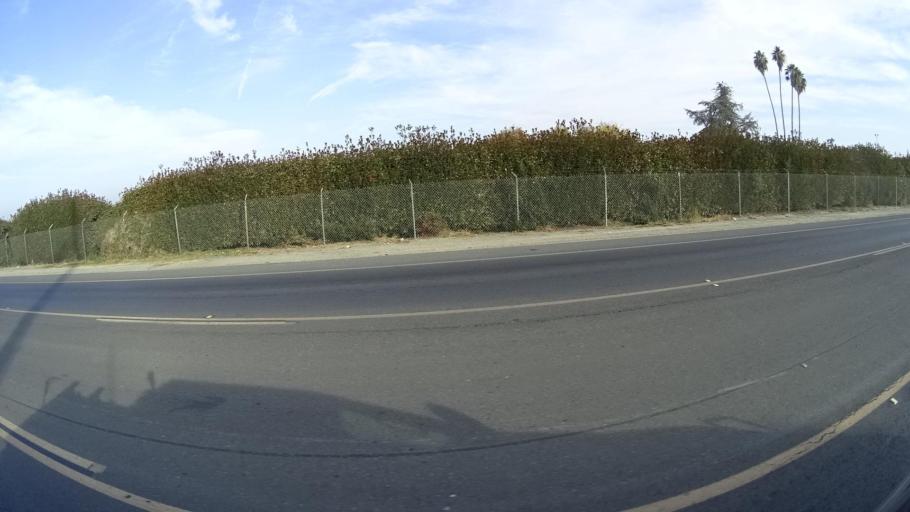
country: US
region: California
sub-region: Kern County
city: Delano
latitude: 35.7903
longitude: -119.2454
